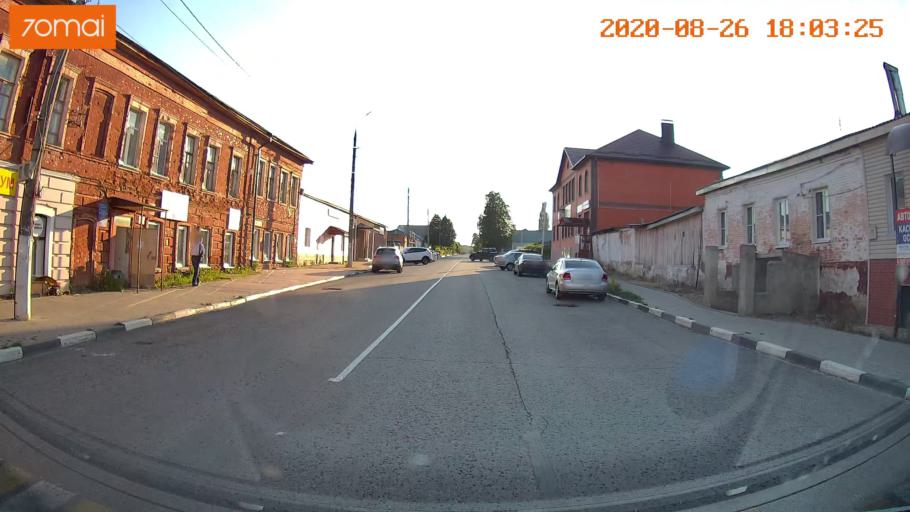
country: RU
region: Tula
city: Yefremov
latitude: 53.1412
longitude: 38.1190
